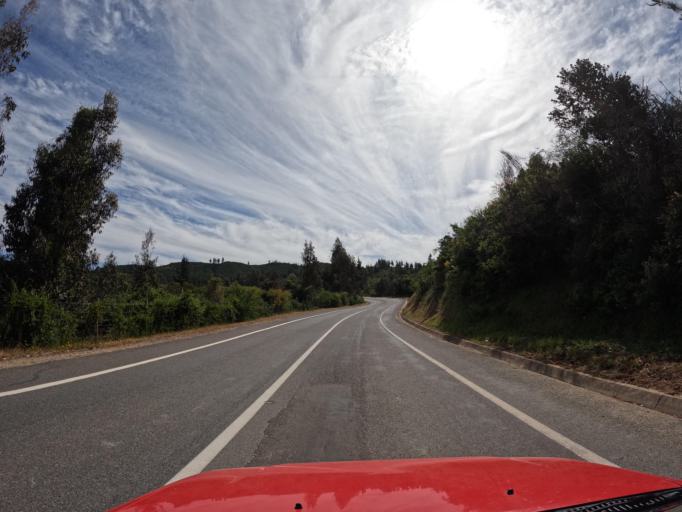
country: CL
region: Maule
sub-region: Provincia de Talca
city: Talca
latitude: -35.1579
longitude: -71.9672
